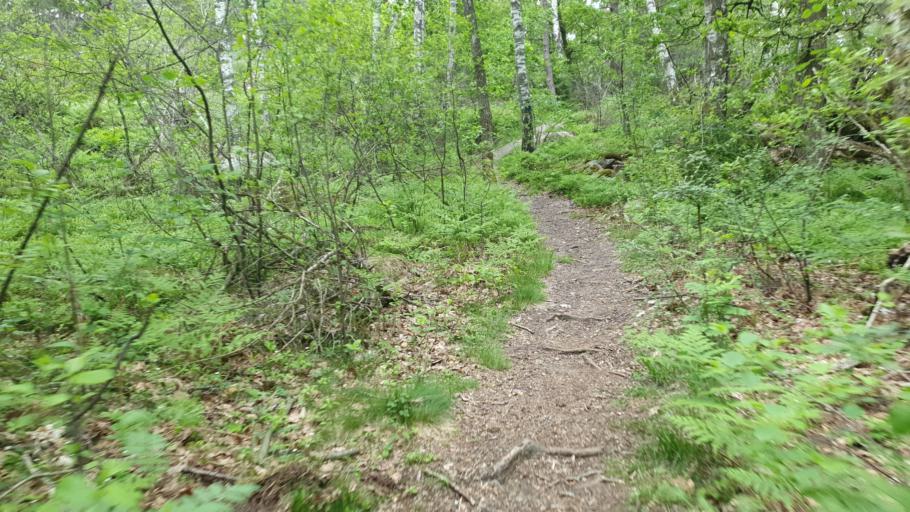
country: SE
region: Vaestra Goetaland
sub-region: Molndal
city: Kallered
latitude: 57.6162
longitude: 12.0528
